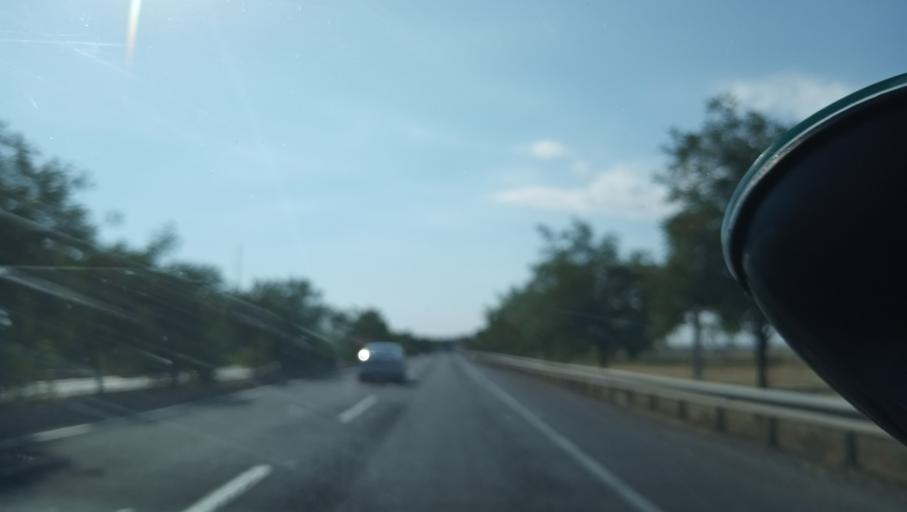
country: TR
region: Diyarbakir
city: Sur
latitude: 37.8207
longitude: 40.3058
